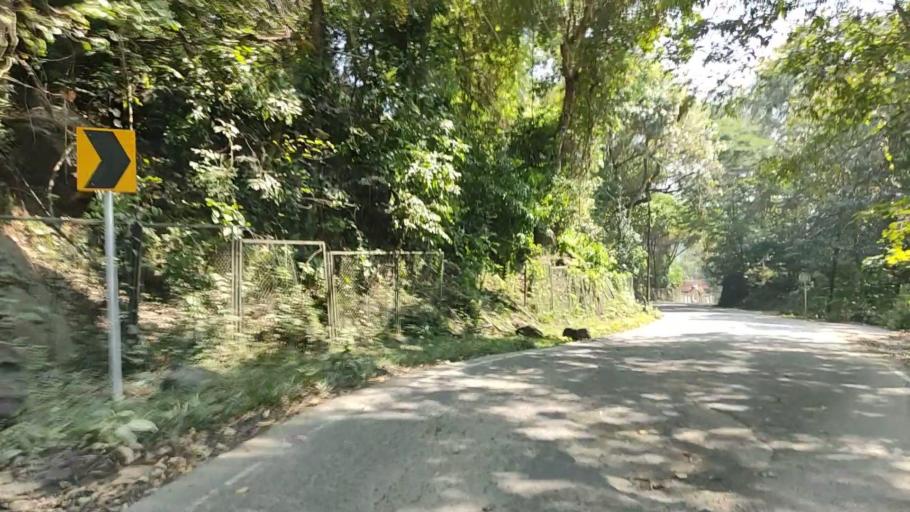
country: IN
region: Kerala
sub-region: Kollam
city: Punalur
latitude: 8.9604
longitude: 77.0676
